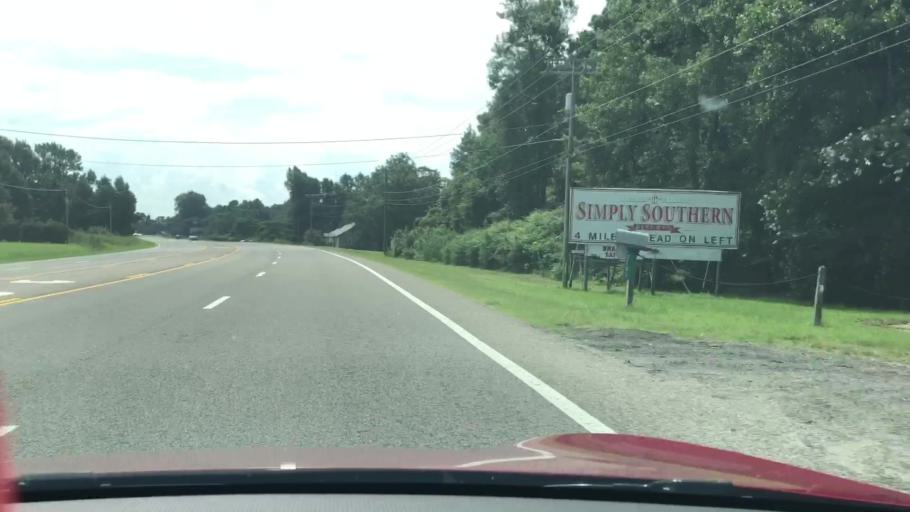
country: US
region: North Carolina
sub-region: Dare County
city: Southern Shores
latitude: 36.1551
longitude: -75.8558
